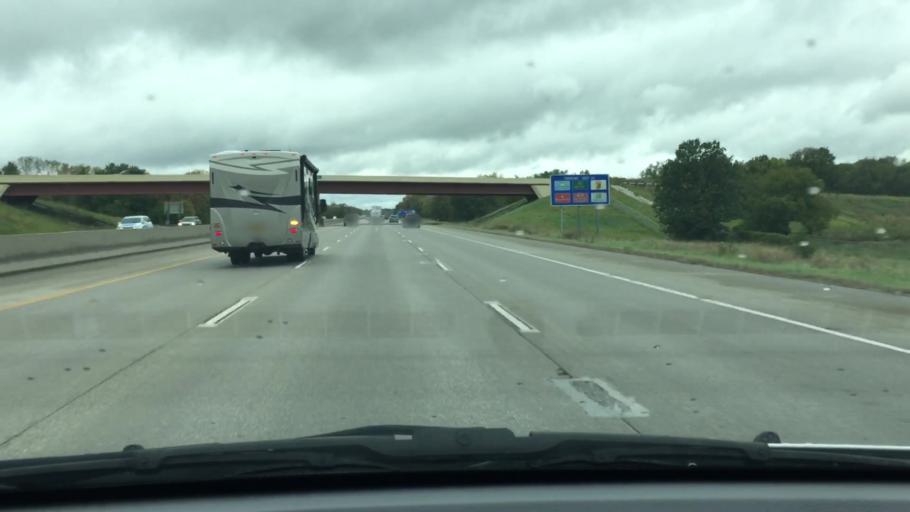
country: US
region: Iowa
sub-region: Polk County
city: Saylorville
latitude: 41.6504
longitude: -93.6506
